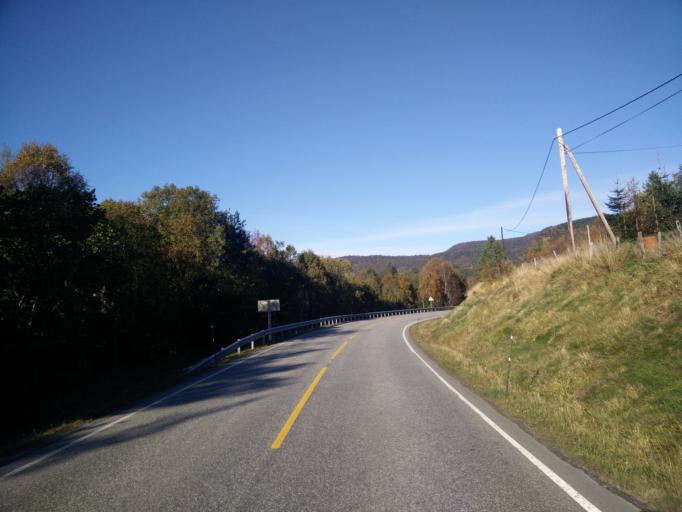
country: NO
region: More og Romsdal
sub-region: Tingvoll
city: Tingvoll
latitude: 63.0409
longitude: 8.0469
